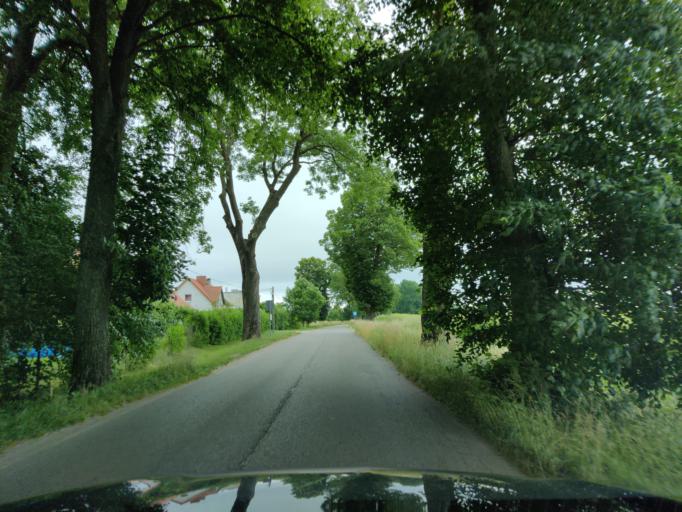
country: PL
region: Warmian-Masurian Voivodeship
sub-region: Powiat gizycki
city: Ryn
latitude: 53.9249
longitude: 21.5521
